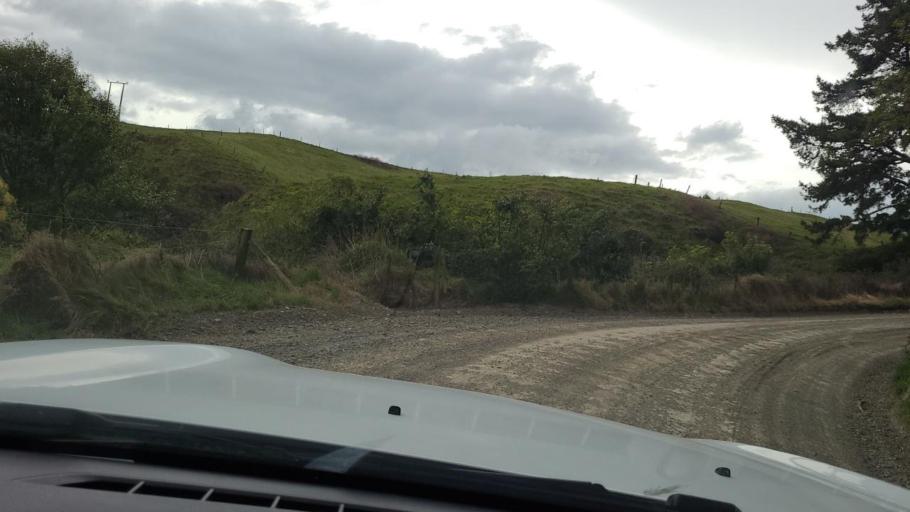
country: NZ
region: Hawke's Bay
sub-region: Napier City
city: Napier
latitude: -39.2654
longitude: 176.8415
